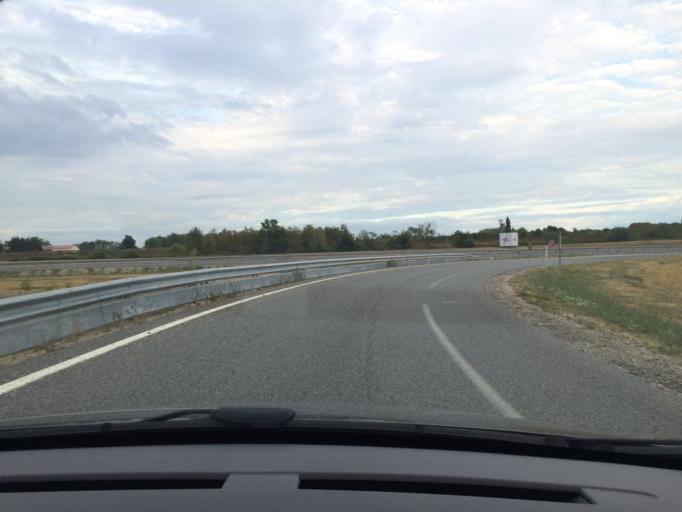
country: FR
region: Rhone-Alpes
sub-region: Departement du Rhone
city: Saint-Laurent-de-Mure
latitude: 45.7010
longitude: 5.0706
